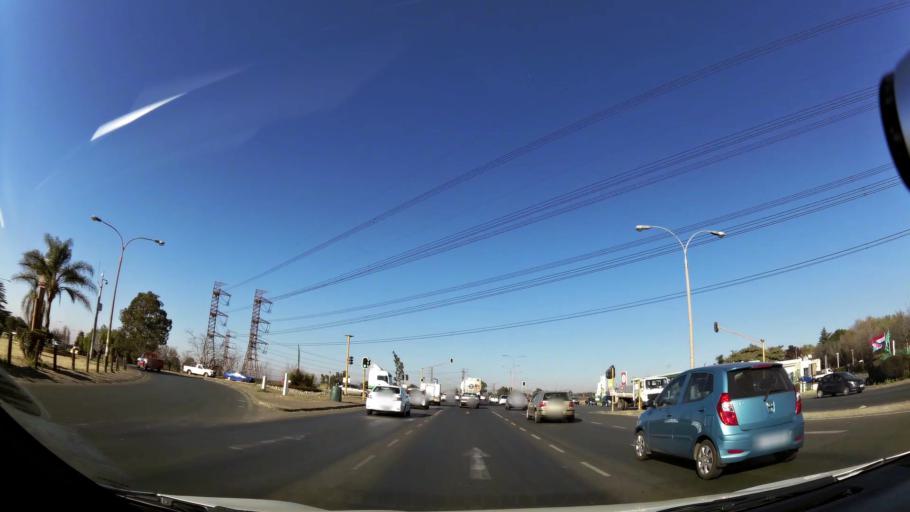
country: ZA
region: Gauteng
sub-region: Ekurhuleni Metropolitan Municipality
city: Germiston
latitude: -26.3010
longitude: 28.1171
